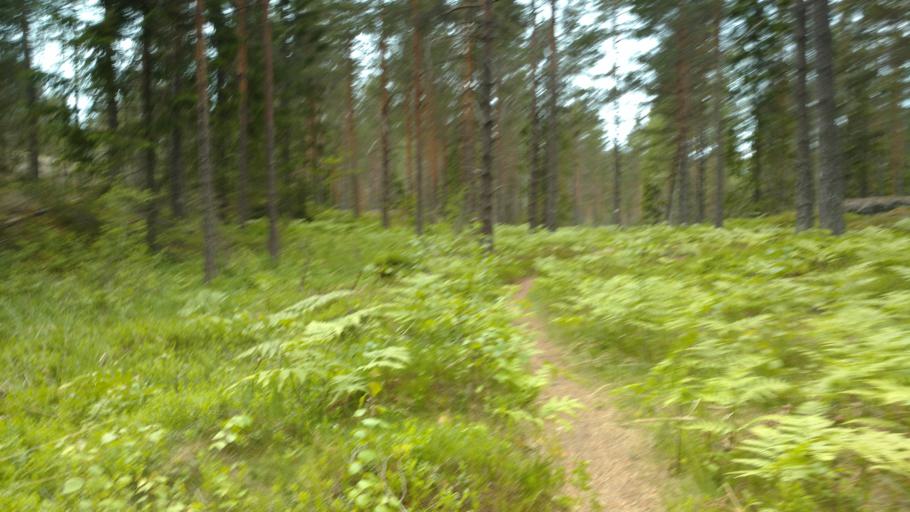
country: FI
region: Uusimaa
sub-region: Raaseporin
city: Pohja
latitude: 60.1159
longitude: 23.5568
